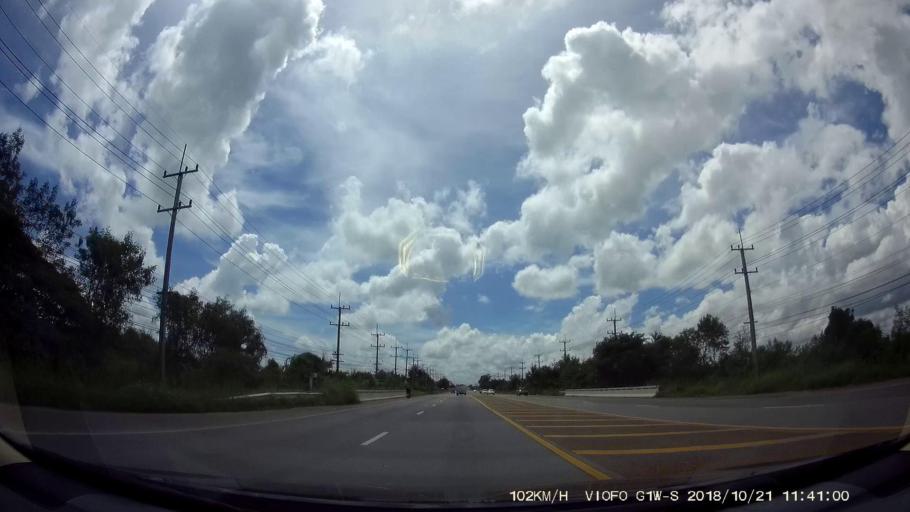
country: TH
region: Chaiyaphum
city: Chaiyaphum
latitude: 15.7056
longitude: 102.0151
